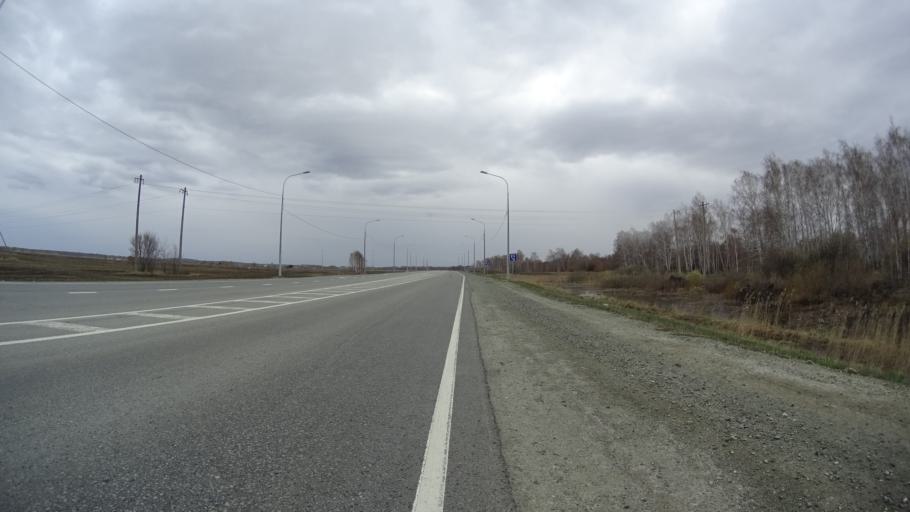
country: RU
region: Chelyabinsk
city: Krasnogorskiy
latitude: 54.6852
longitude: 61.2475
